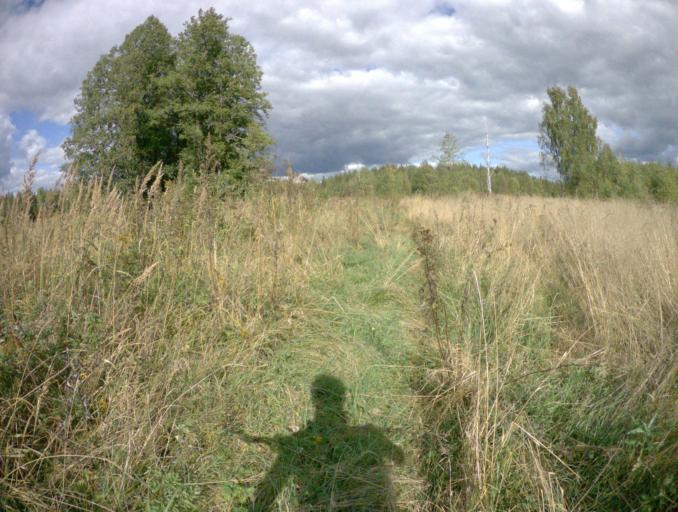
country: RU
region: Vladimir
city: Golovino
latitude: 55.8900
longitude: 40.4245
